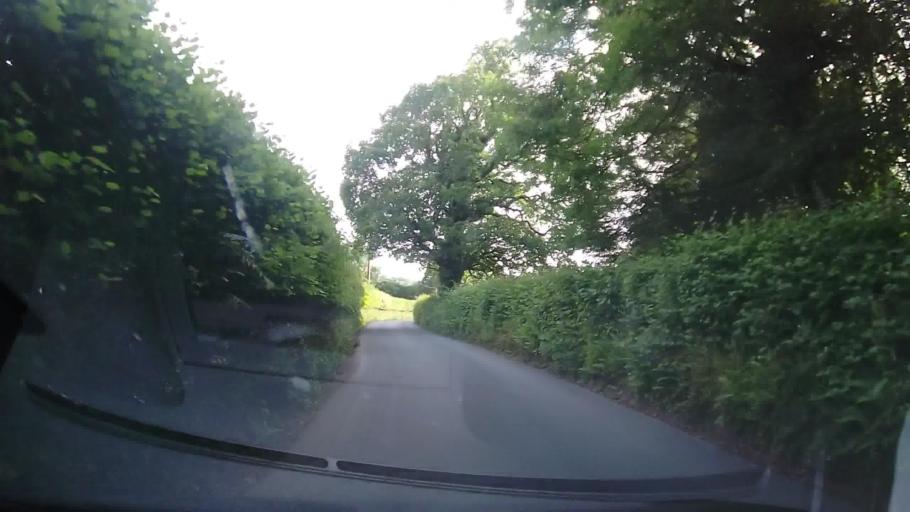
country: GB
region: Wales
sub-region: Gwynedd
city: Bala
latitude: 52.8816
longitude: -3.6226
